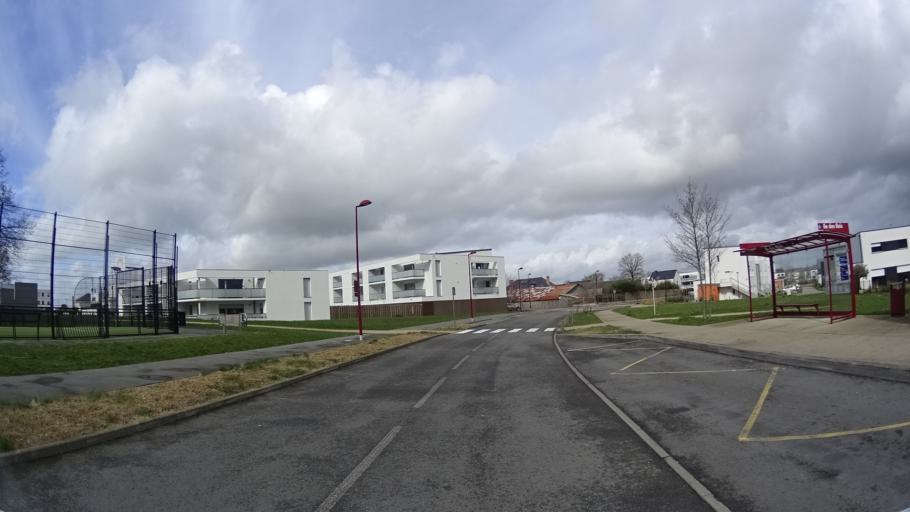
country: FR
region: Brittany
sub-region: Departement d'Ille-et-Vilaine
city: Saint-Gilles
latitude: 48.1496
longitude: -1.8387
